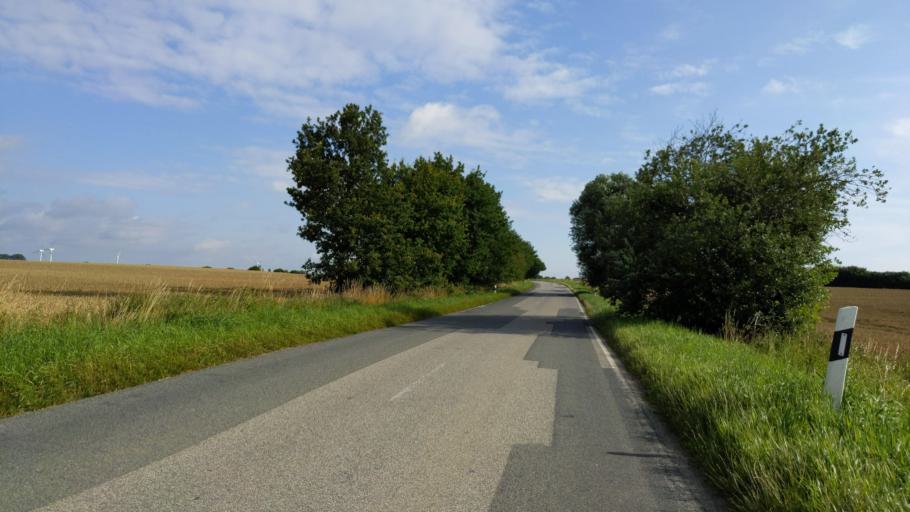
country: DE
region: Schleswig-Holstein
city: Bad Schwartau
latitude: 53.9829
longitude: 10.6593
